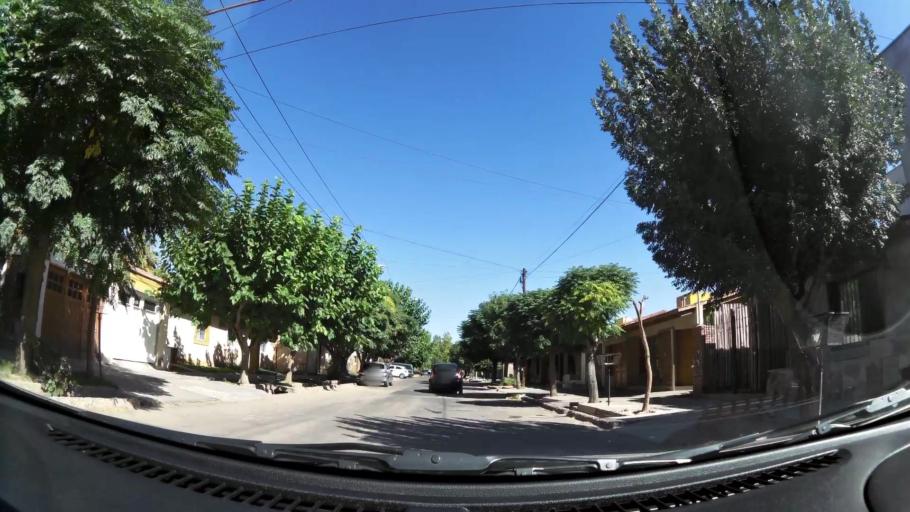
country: AR
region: Mendoza
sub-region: Departamento de Maipu
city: Maipu
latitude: -32.9732
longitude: -68.7990
